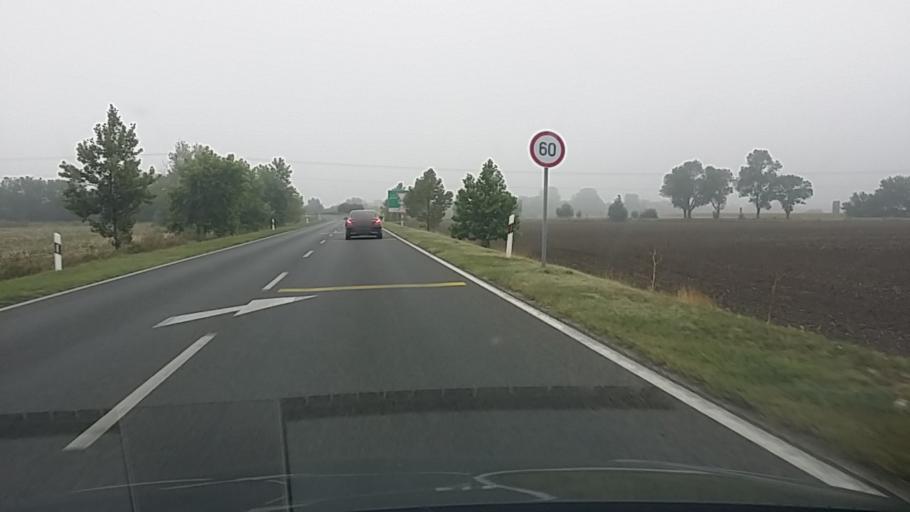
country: HU
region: Csongrad
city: Szeged
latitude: 46.2346
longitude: 20.0871
